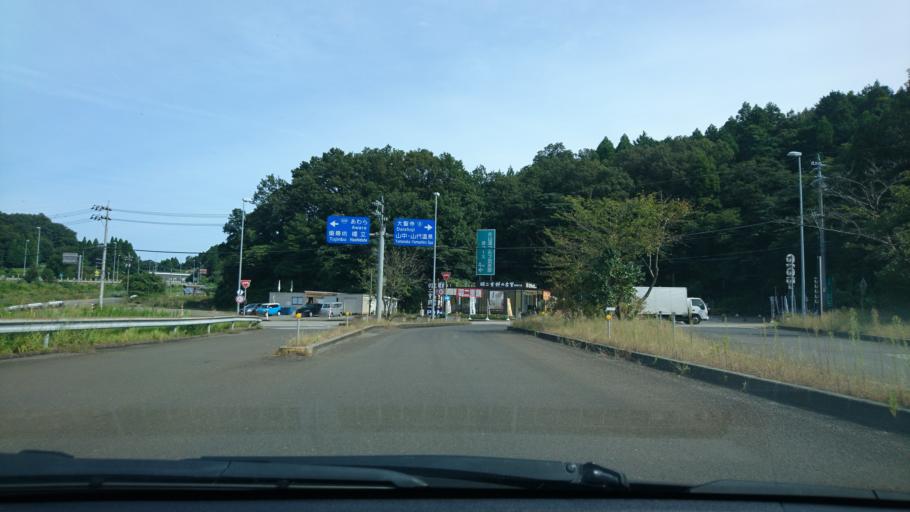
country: JP
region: Fukui
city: Maruoka
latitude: 36.2925
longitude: 136.2904
